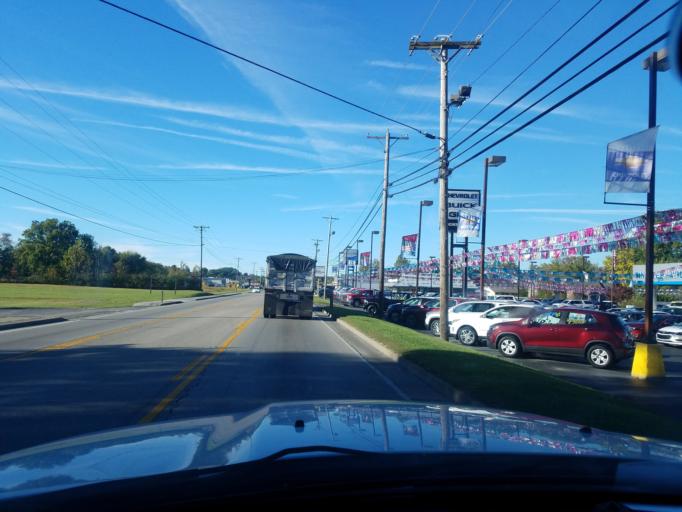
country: US
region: Kentucky
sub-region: Laurel County
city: London
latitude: 37.0975
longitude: -84.0674
